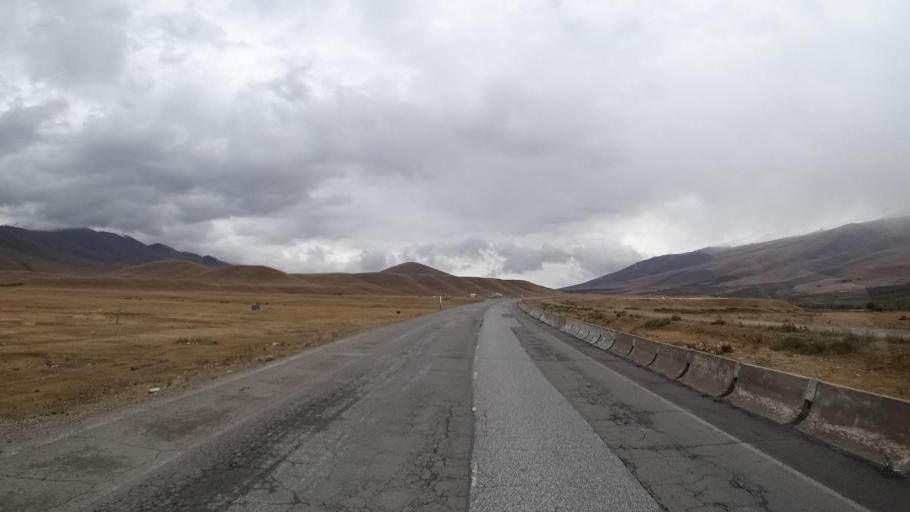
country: KG
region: Jalal-Abad
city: Uch-Terek
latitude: 42.1941
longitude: 73.5266
